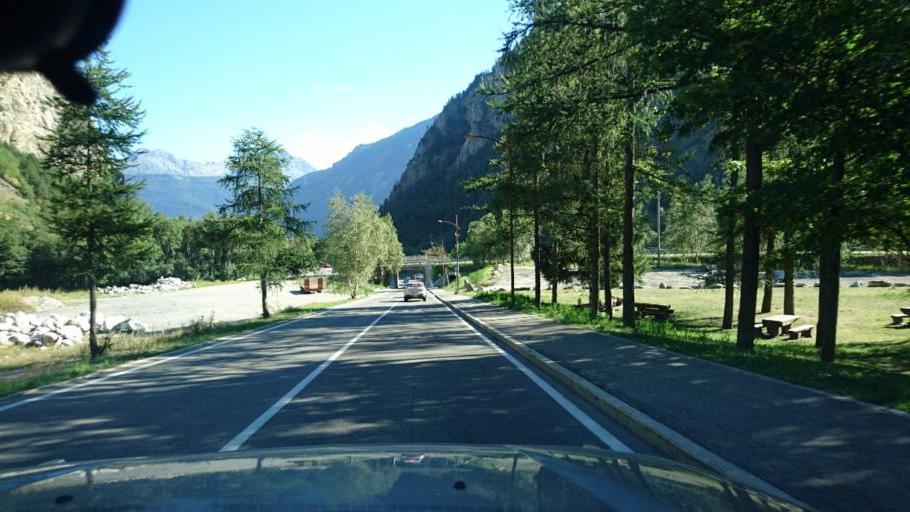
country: IT
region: Aosta Valley
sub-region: Valle d'Aosta
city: Courmayeur
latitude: 45.8113
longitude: 6.9636
